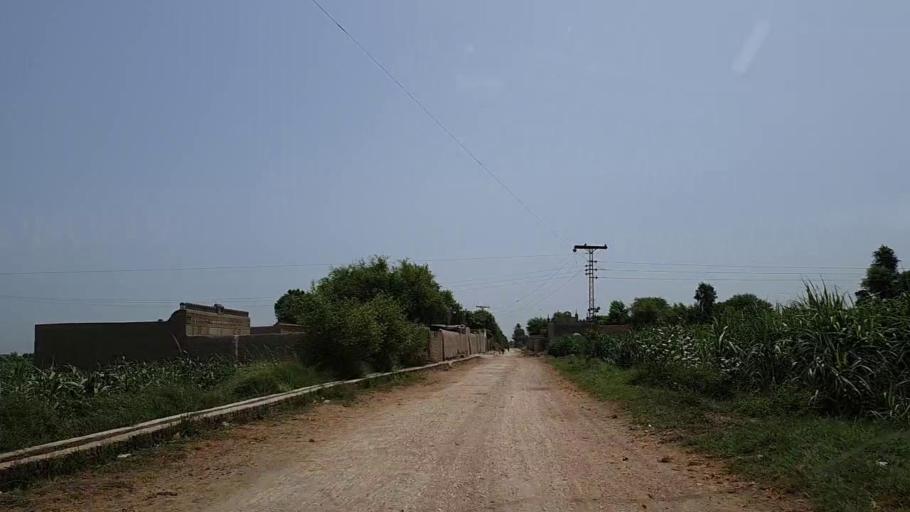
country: PK
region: Sindh
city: Naushahro Firoz
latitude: 26.8425
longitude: 67.9786
